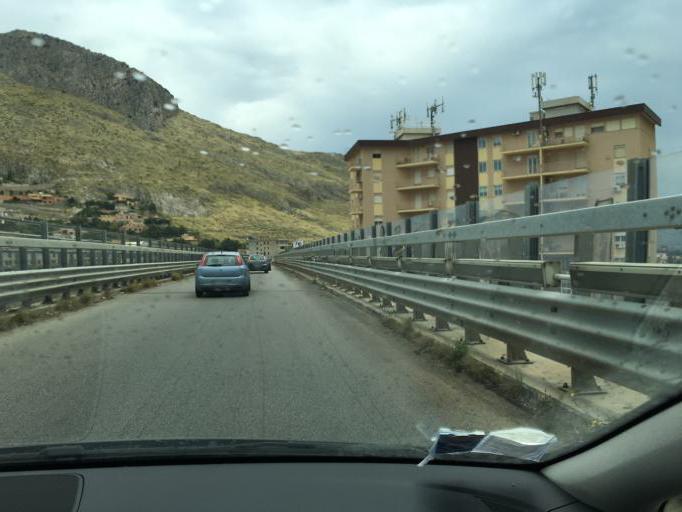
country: IT
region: Sicily
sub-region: Palermo
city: Isola delle Femmine
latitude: 38.1913
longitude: 13.2844
